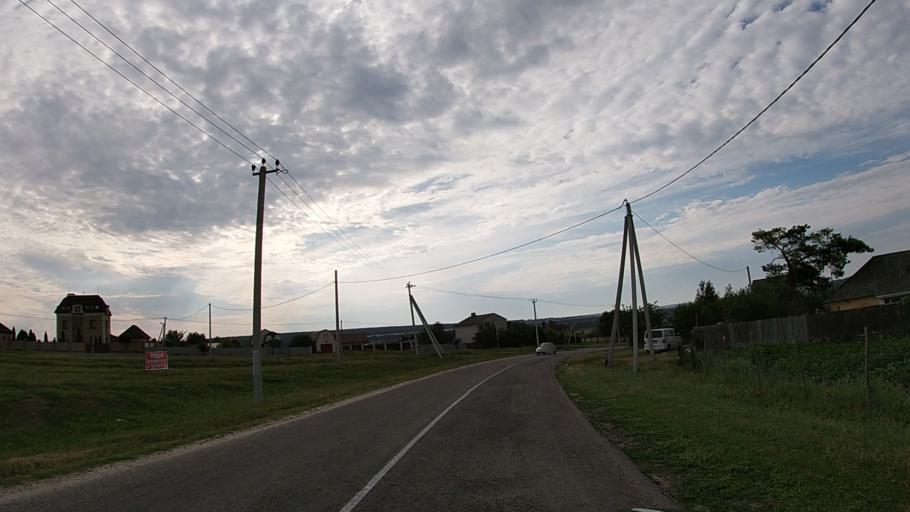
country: RU
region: Belgorod
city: Severnyy
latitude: 50.7145
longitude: 36.5940
